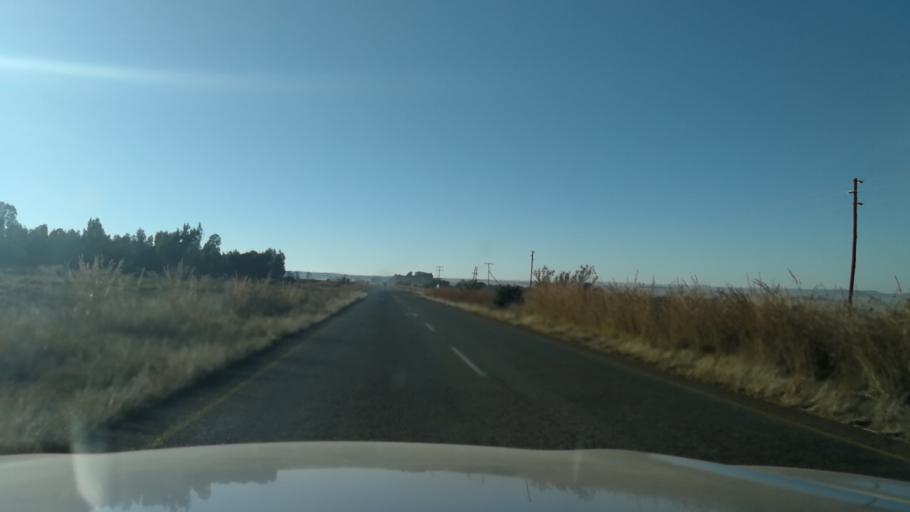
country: ZA
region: North-West
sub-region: Bojanala Platinum District Municipality
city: Koster
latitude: -25.9207
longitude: 27.0905
